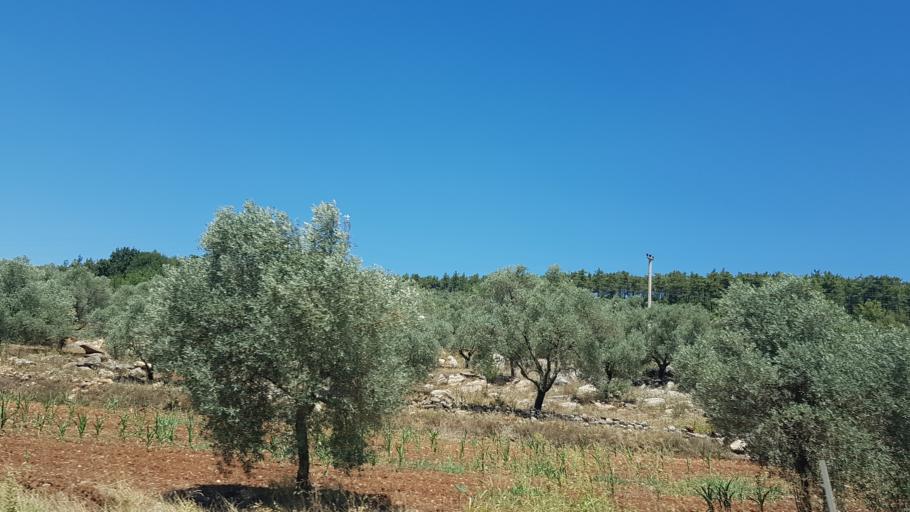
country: TR
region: Mugla
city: Turgut
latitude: 37.3077
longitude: 27.9976
